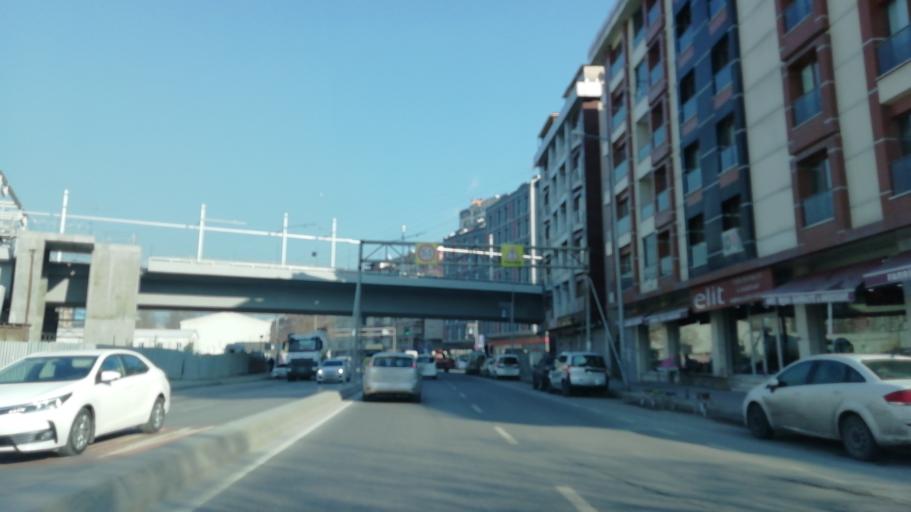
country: TR
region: Istanbul
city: Sisli
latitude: 41.0785
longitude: 28.9507
